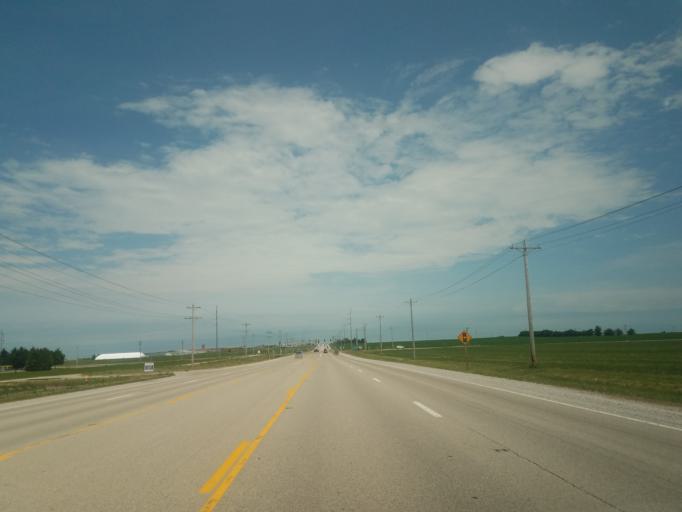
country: US
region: Illinois
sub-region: McLean County
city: Downs
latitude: 40.4557
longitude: -88.9018
